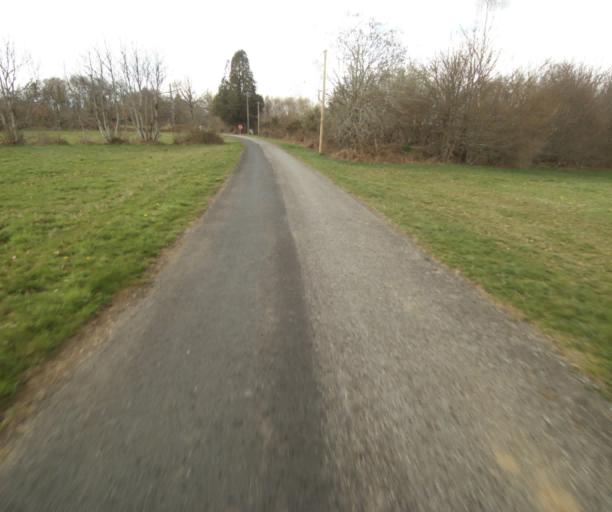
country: FR
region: Limousin
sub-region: Departement de la Correze
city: Egletons
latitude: 45.2603
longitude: 1.9922
